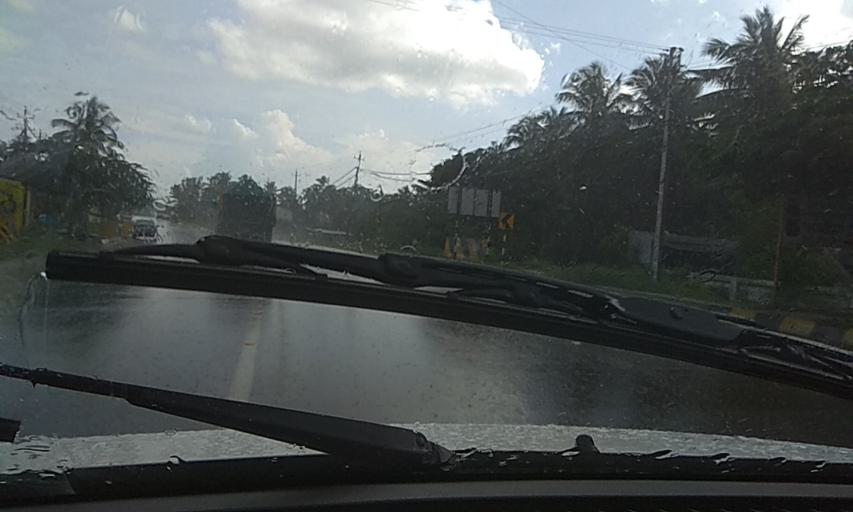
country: IN
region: Karnataka
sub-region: Mandya
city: Maddur
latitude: 12.6900
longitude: 77.0594
